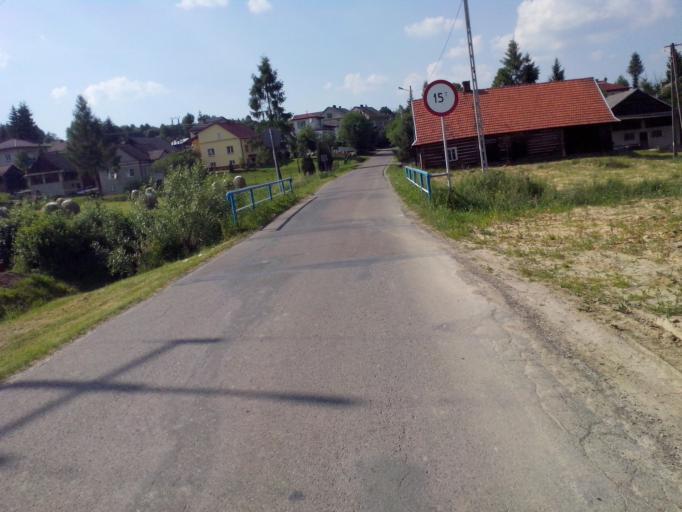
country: PL
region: Subcarpathian Voivodeship
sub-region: Powiat brzozowski
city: Blizne
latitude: 49.7407
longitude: 21.9755
